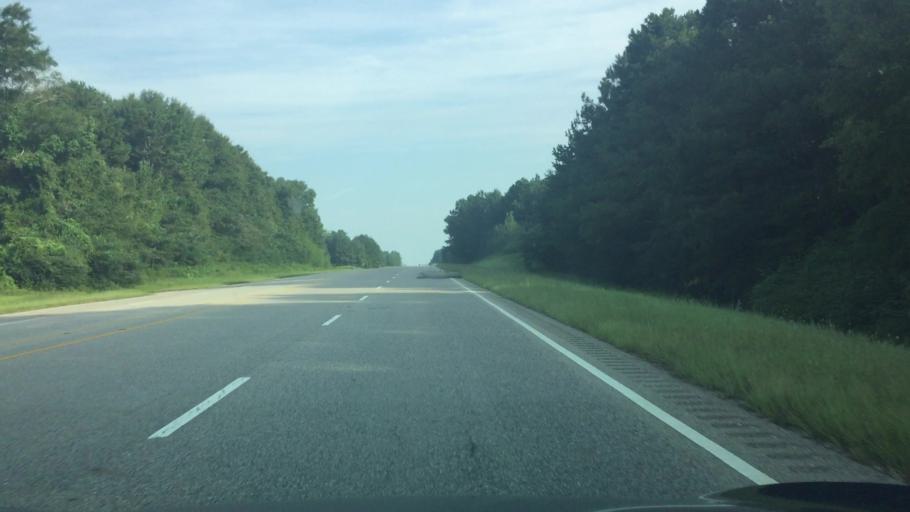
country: US
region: Alabama
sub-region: Butler County
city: Georgiana
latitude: 31.4739
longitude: -86.6697
